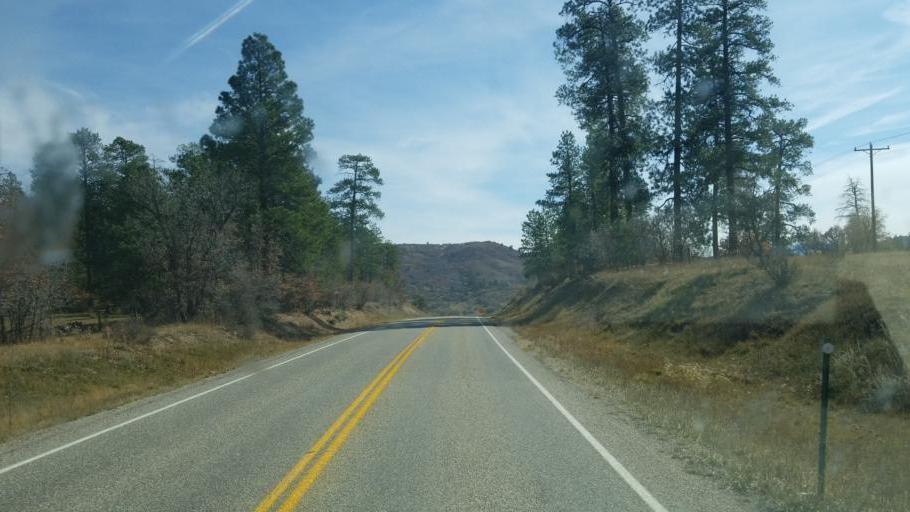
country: US
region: New Mexico
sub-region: Rio Arriba County
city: Dulce
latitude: 37.0745
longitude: -106.8359
